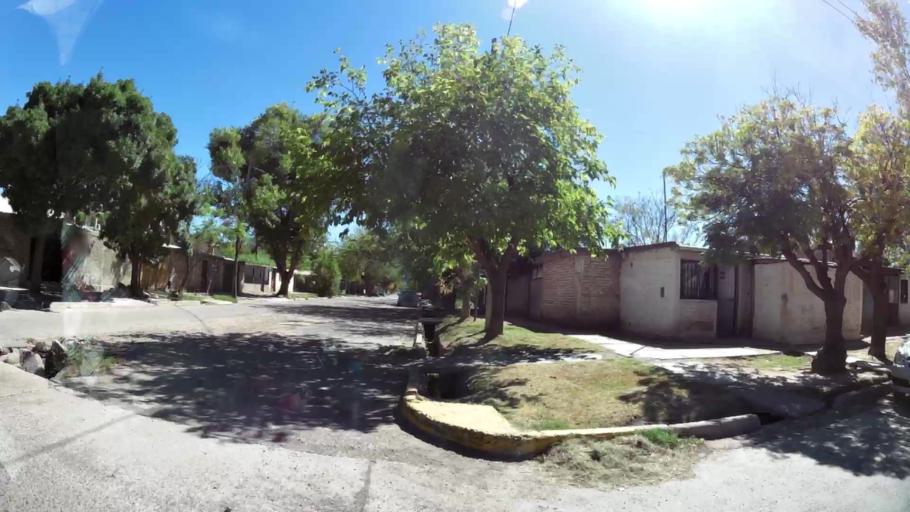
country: AR
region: Mendoza
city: Las Heras
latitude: -32.8297
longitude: -68.8224
